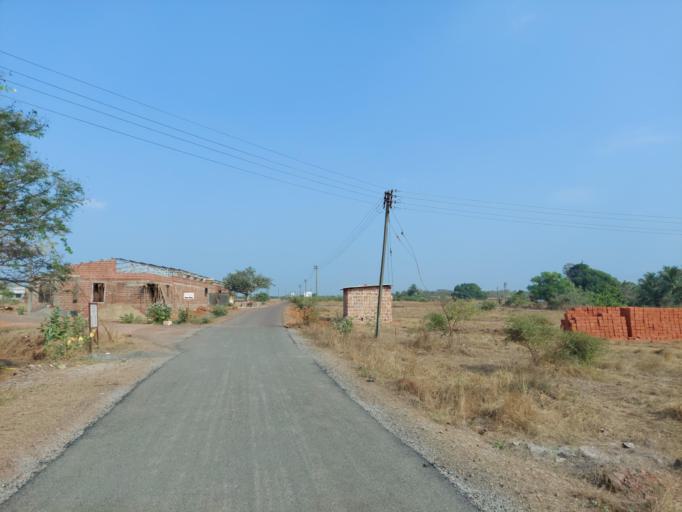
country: IN
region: Maharashtra
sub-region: Ratnagiri
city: Ratnagiri
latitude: 16.9326
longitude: 73.3248
